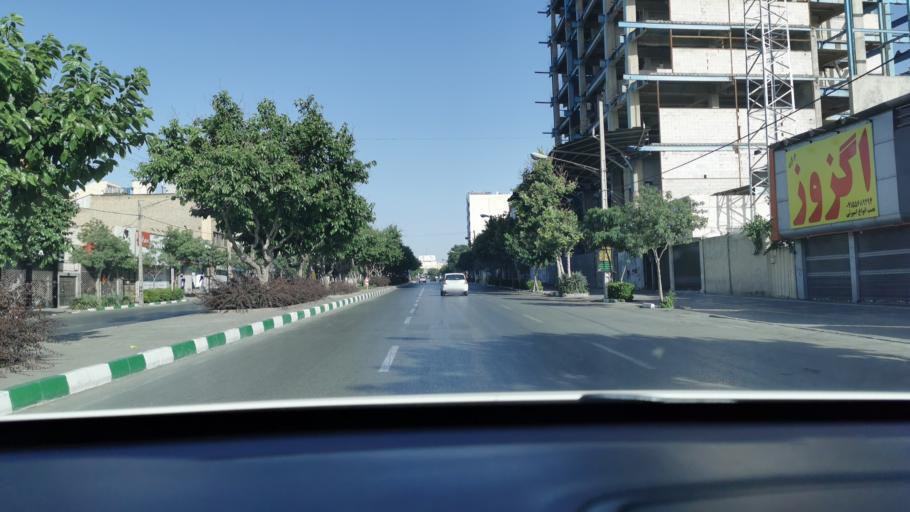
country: IR
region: Razavi Khorasan
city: Mashhad
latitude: 36.3322
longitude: 59.5166
